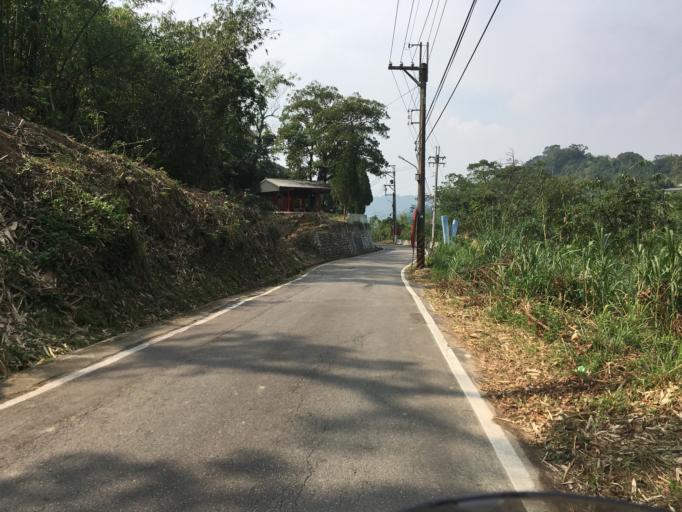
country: TW
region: Taiwan
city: Fengyuan
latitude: 24.1849
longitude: 120.7638
